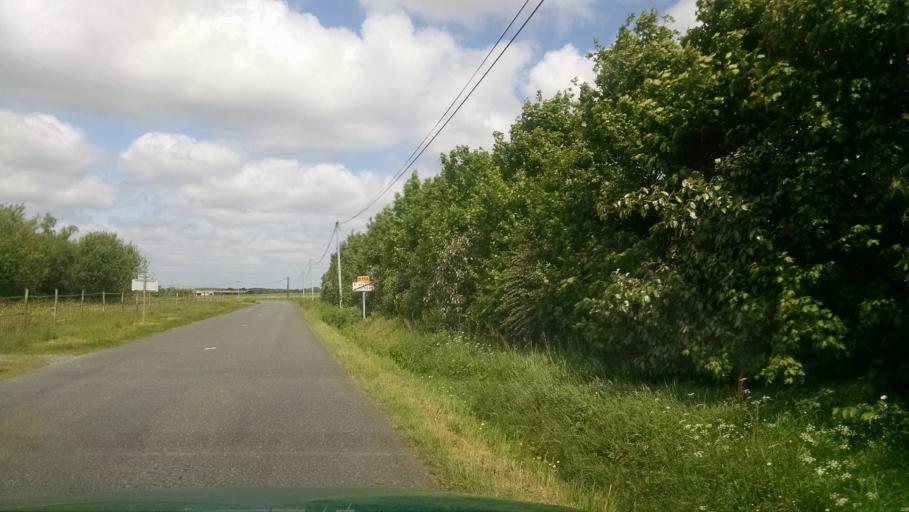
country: FR
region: Pays de la Loire
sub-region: Departement de la Loire-Atlantique
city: Saint-Hilaire-de-Clisson
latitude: 47.0680
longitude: -1.3077
